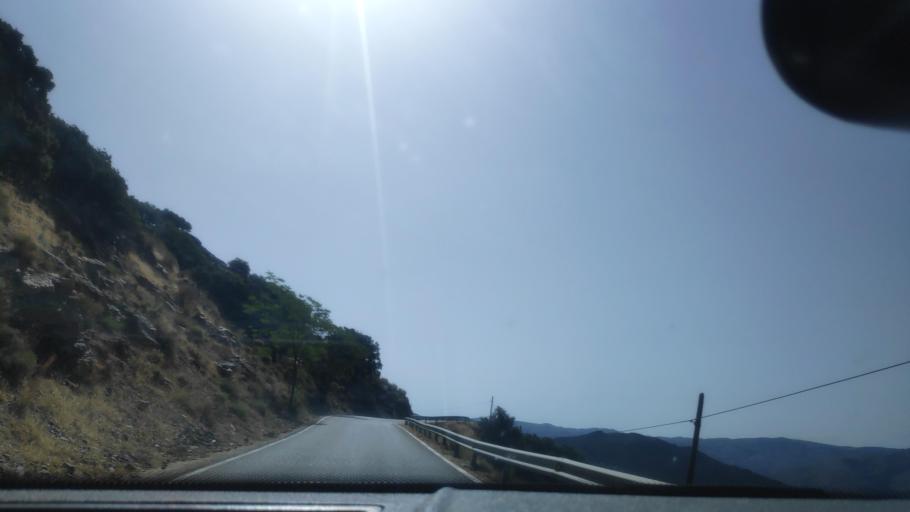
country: ES
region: Andalusia
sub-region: Provincia de Granada
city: Pampaneira
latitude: 36.9270
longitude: -3.3659
